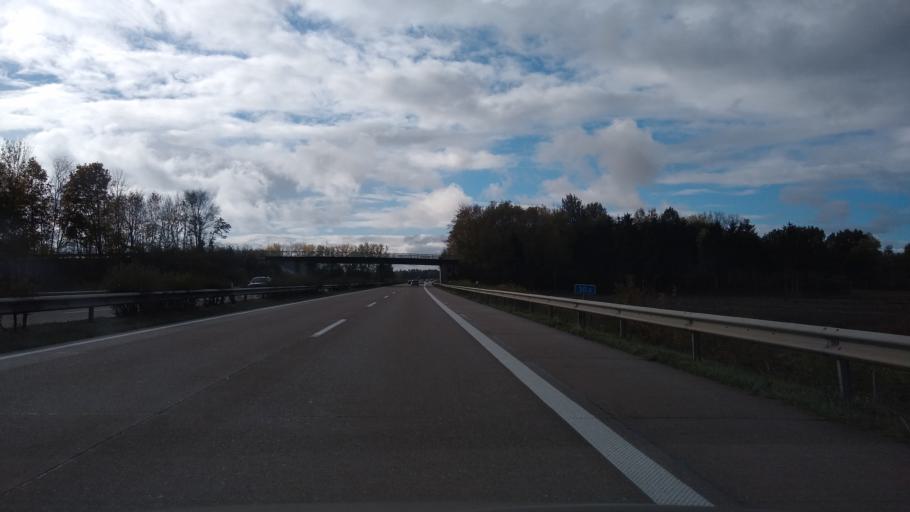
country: DE
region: Lower Saxony
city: Oldenburg
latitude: 53.0954
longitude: 8.2646
